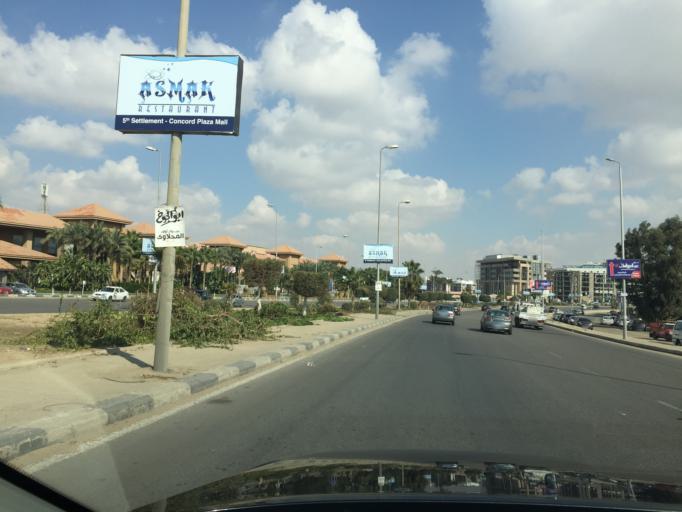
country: EG
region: Muhafazat al Qalyubiyah
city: Al Khankah
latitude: 30.0239
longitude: 31.4547
